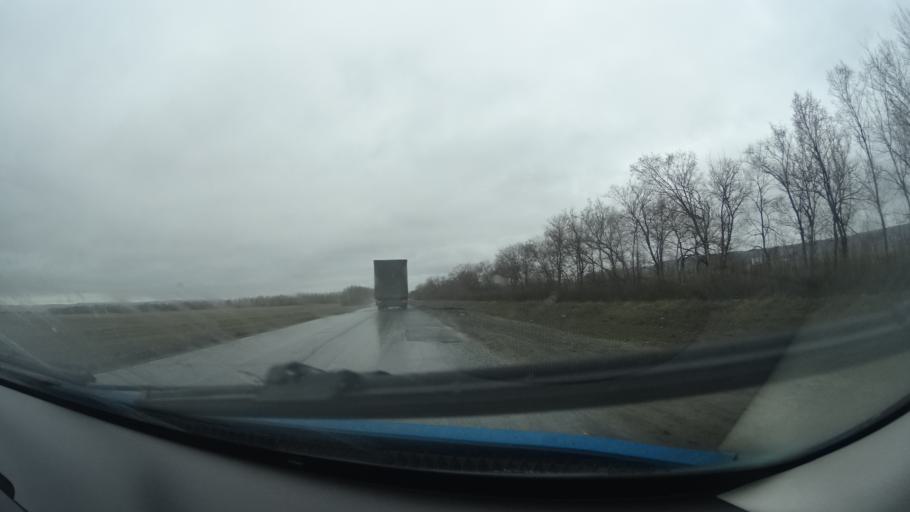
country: RU
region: Bashkortostan
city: Kandry
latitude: 54.5346
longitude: 54.1119
